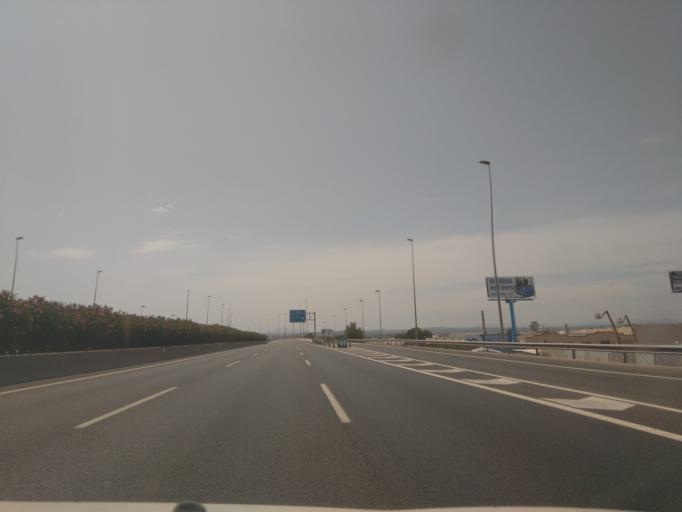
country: ES
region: Valencia
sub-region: Provincia de Valencia
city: Beniparrell
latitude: 39.3768
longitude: -0.4099
